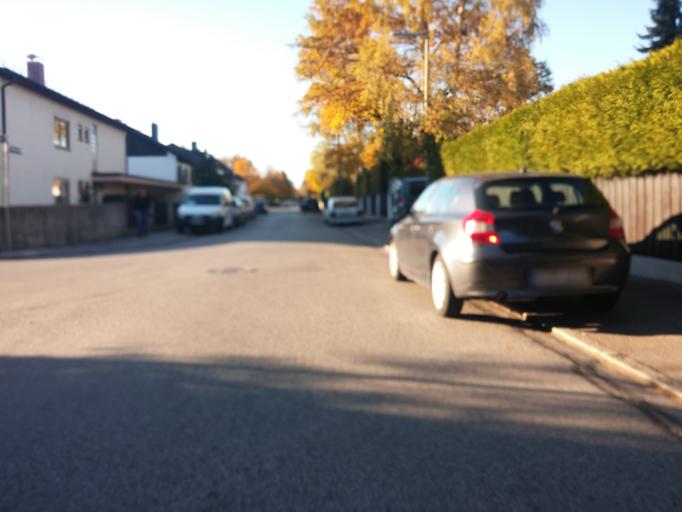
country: DE
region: Bavaria
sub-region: Upper Bavaria
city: Haar
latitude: 48.1080
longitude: 11.7087
